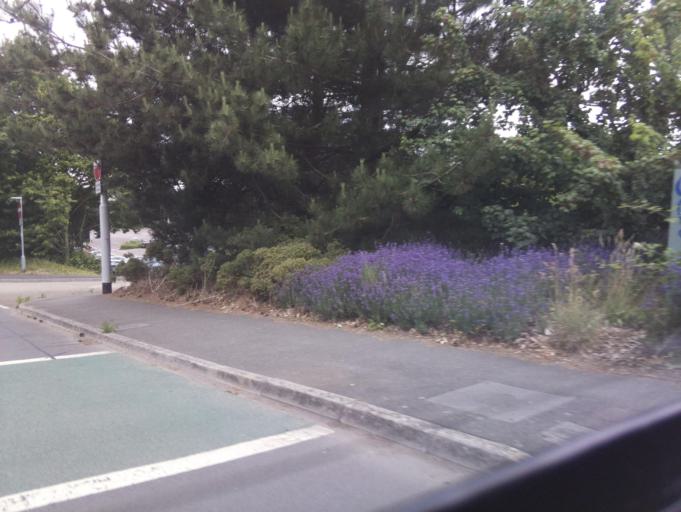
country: GB
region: England
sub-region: Devon
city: Heavitree
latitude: 50.7155
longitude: -3.4707
